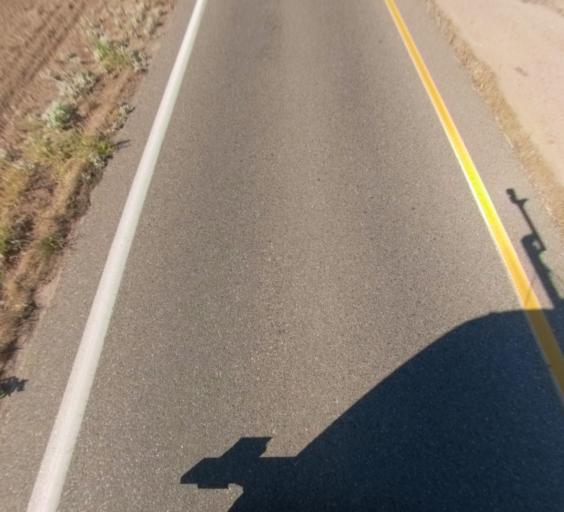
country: US
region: California
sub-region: Fresno County
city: Clovis
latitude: 36.8825
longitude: -119.8071
